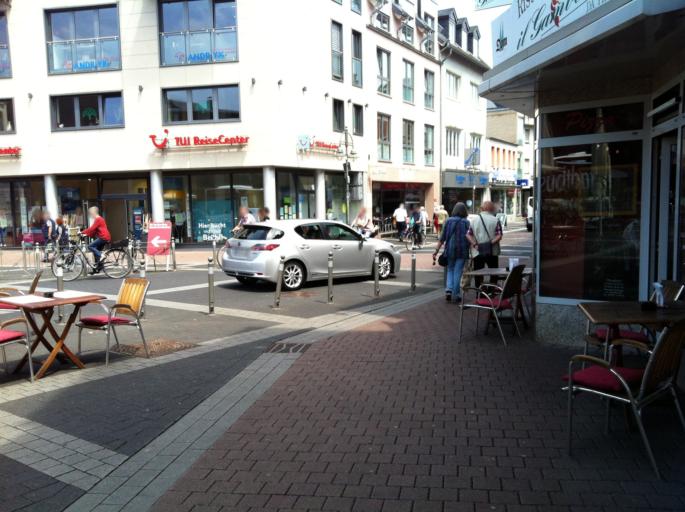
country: DE
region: North Rhine-Westphalia
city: Bruhl
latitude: 50.8264
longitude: 6.9018
